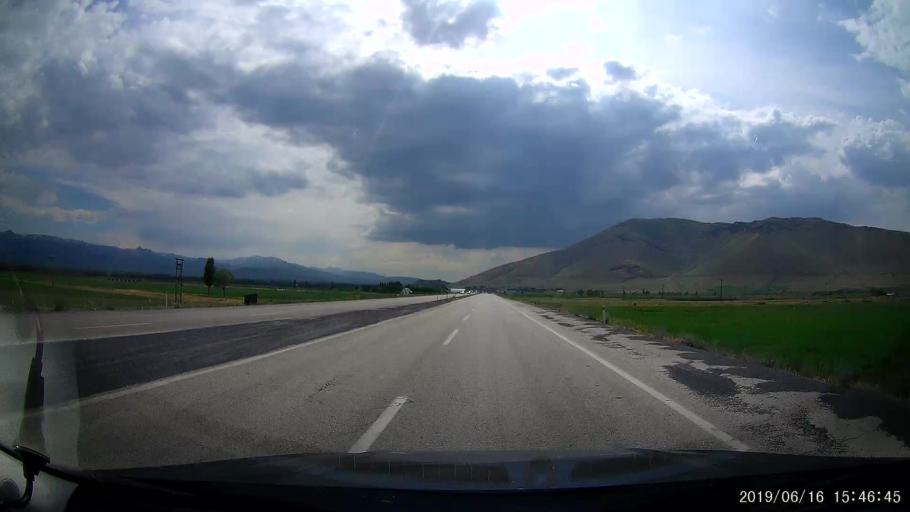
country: TR
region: Erzurum
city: Pasinler
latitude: 39.9895
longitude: 41.7367
